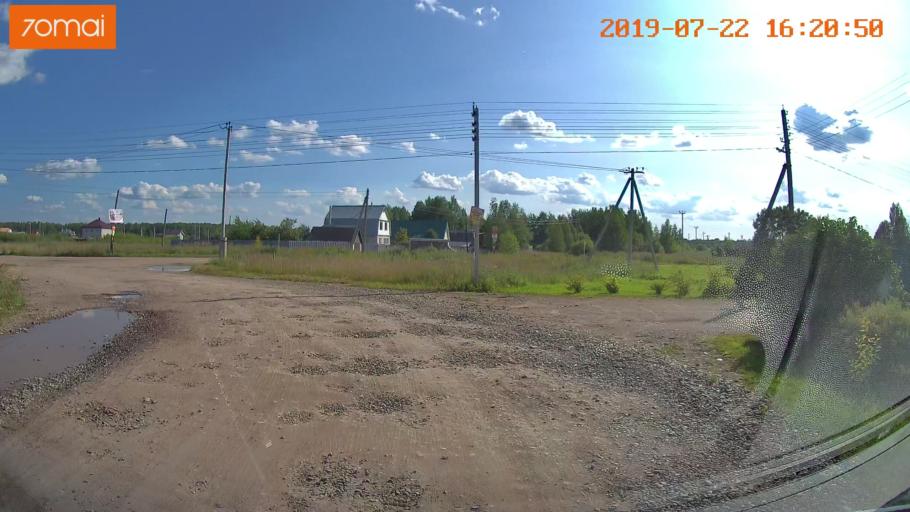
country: RU
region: Ivanovo
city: Novo-Talitsy
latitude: 57.0637
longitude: 40.8911
